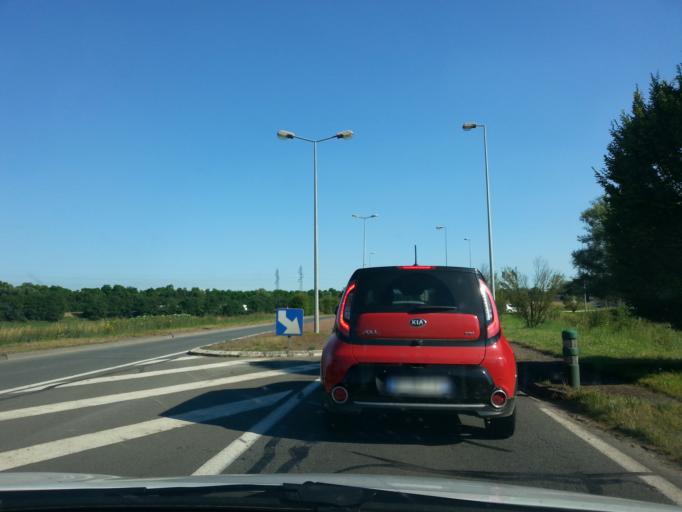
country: FR
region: Rhone-Alpes
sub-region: Departement du Rhone
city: Belleville
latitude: 46.1099
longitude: 4.7549
